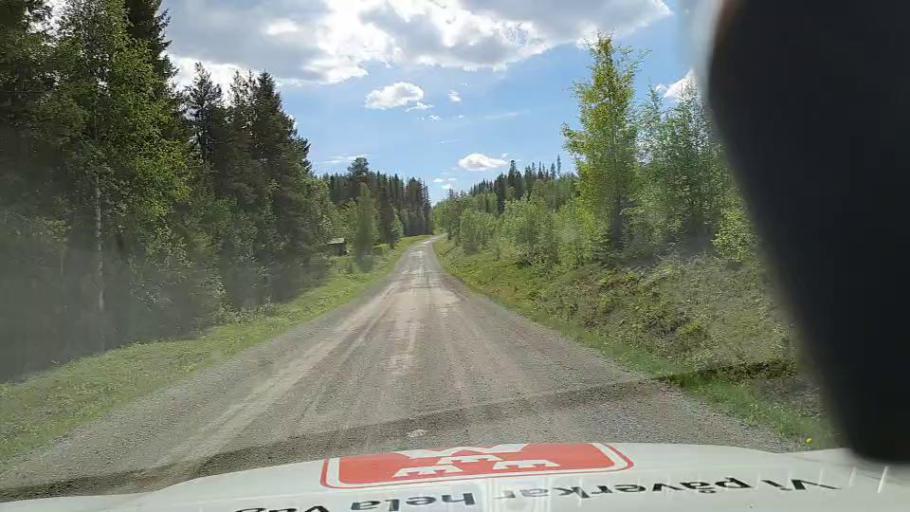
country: SE
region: Vaesterbotten
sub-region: Vilhelmina Kommun
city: Sjoberg
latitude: 64.5659
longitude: 15.8517
